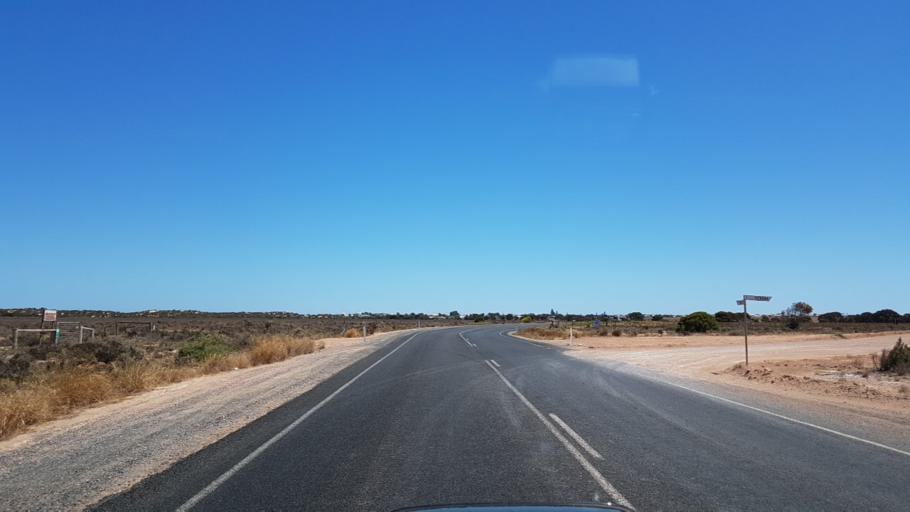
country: AU
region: South Australia
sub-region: Copper Coast
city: Wallaroo
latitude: -33.9133
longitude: 137.6449
